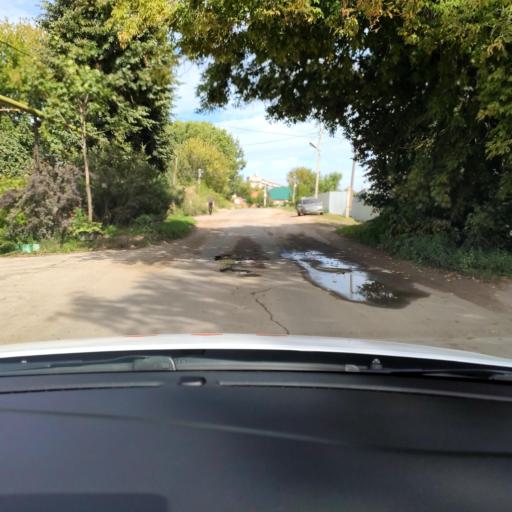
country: RU
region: Tatarstan
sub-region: Gorod Kazan'
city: Kazan
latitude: 55.7166
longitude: 49.0912
